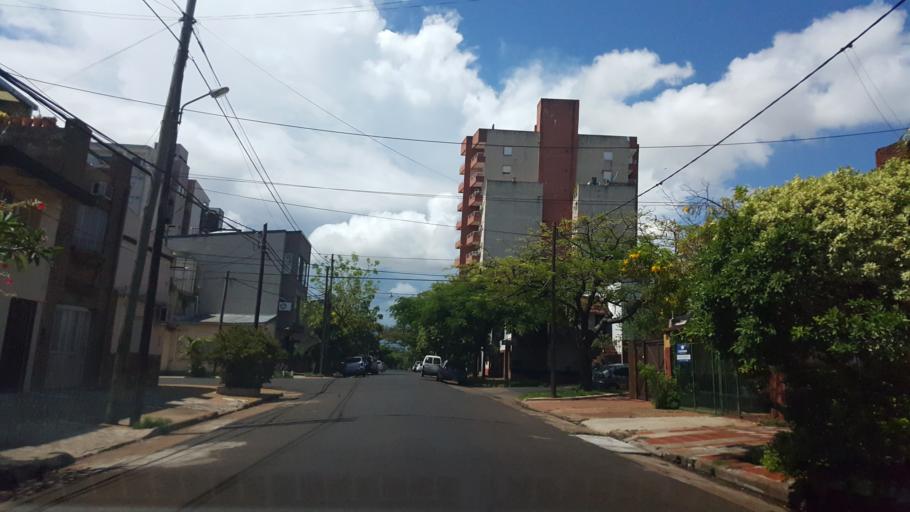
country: AR
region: Misiones
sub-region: Departamento de Capital
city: Posadas
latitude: -27.3572
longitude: -55.8975
